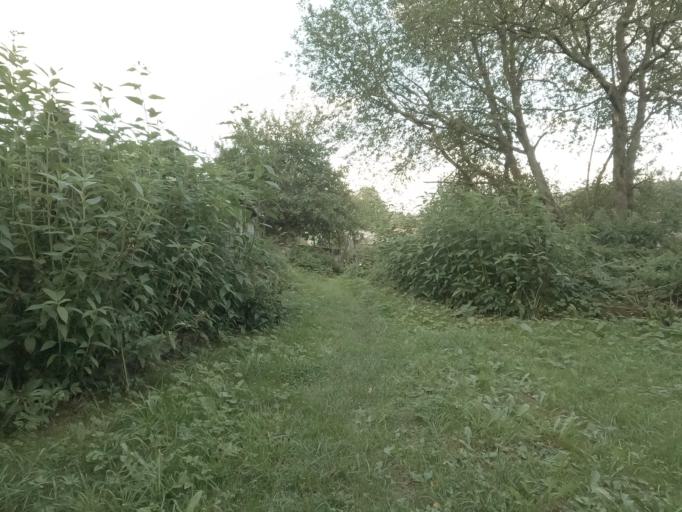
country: RU
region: Leningrad
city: Mga
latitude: 59.7514
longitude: 31.0355
